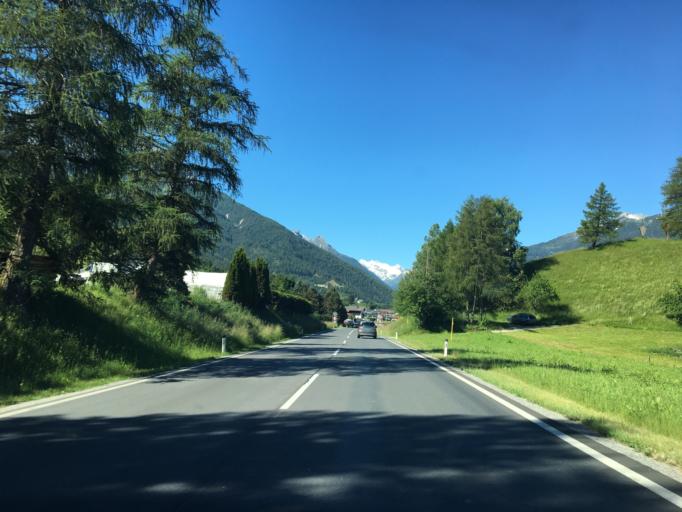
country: AT
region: Tyrol
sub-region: Politischer Bezirk Innsbruck Land
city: Mieders
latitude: 47.1758
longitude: 11.3900
